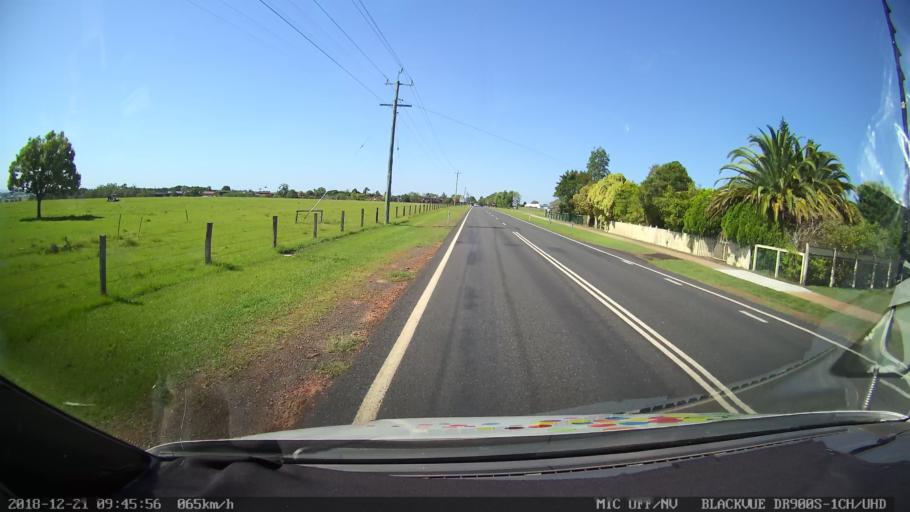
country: AU
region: New South Wales
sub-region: Clarence Valley
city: Grafton
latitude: -29.6344
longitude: 152.9274
